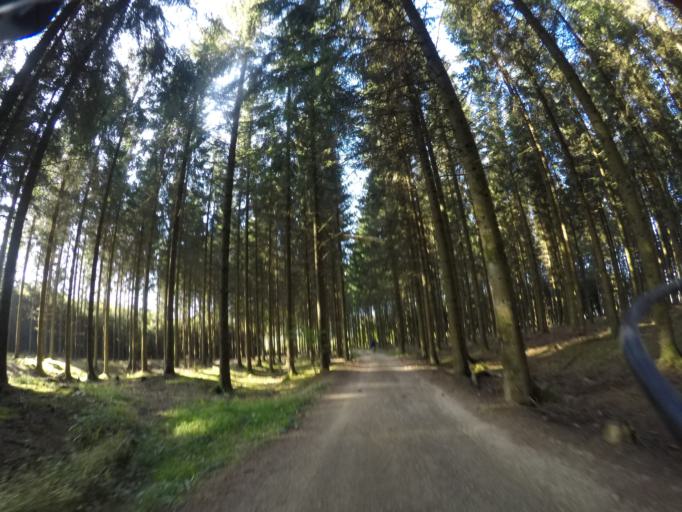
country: BE
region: Wallonia
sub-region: Province du Luxembourg
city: Fauvillers
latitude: 49.9291
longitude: 5.6578
